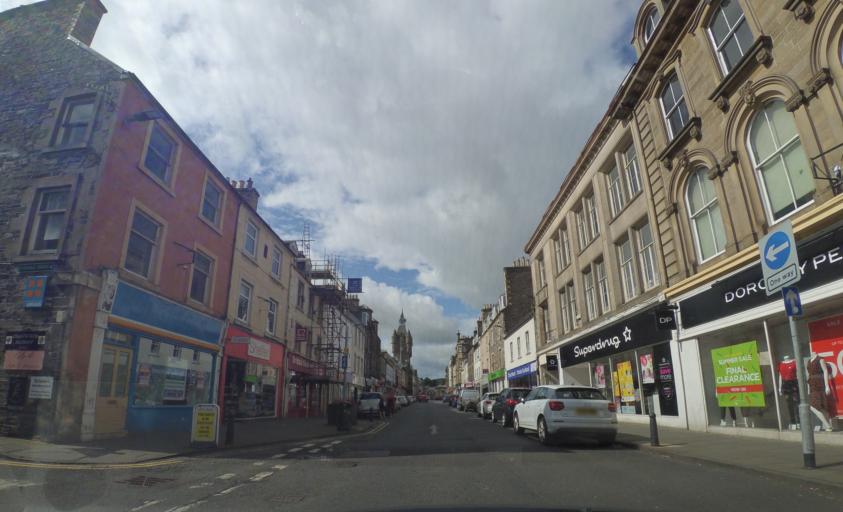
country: GB
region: Scotland
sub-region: The Scottish Borders
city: Hawick
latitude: 55.4239
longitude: -2.7855
